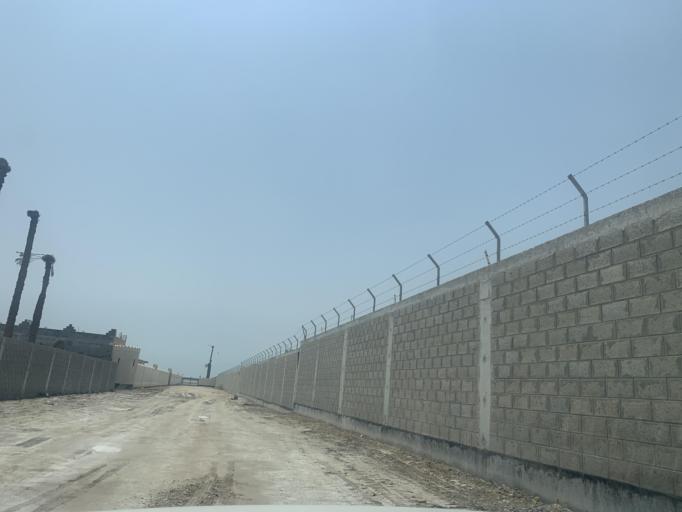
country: BH
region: Central Governorate
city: Madinat Hamad
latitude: 26.1290
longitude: 50.4626
